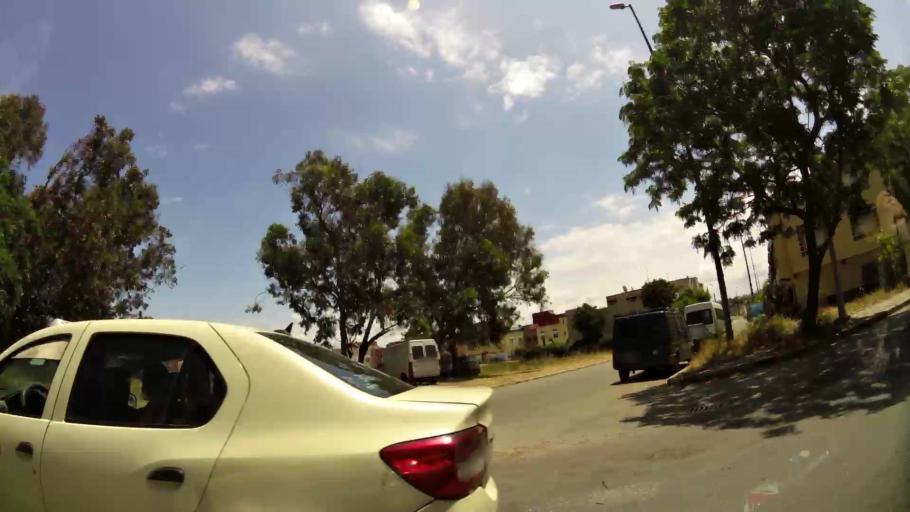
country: MA
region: Gharb-Chrarda-Beni Hssen
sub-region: Kenitra Province
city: Kenitra
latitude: 34.2615
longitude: -6.6125
